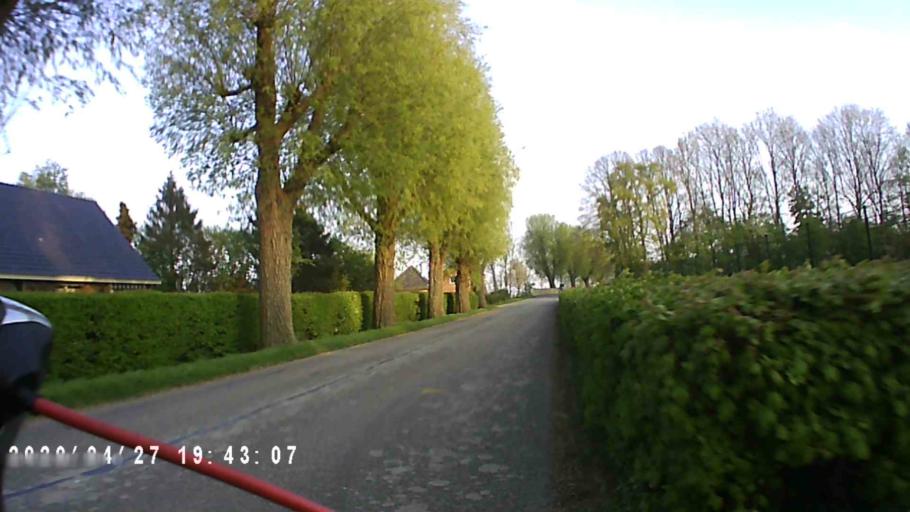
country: NL
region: Groningen
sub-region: Gemeente Winsum
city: Winsum
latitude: 53.3565
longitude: 6.4650
